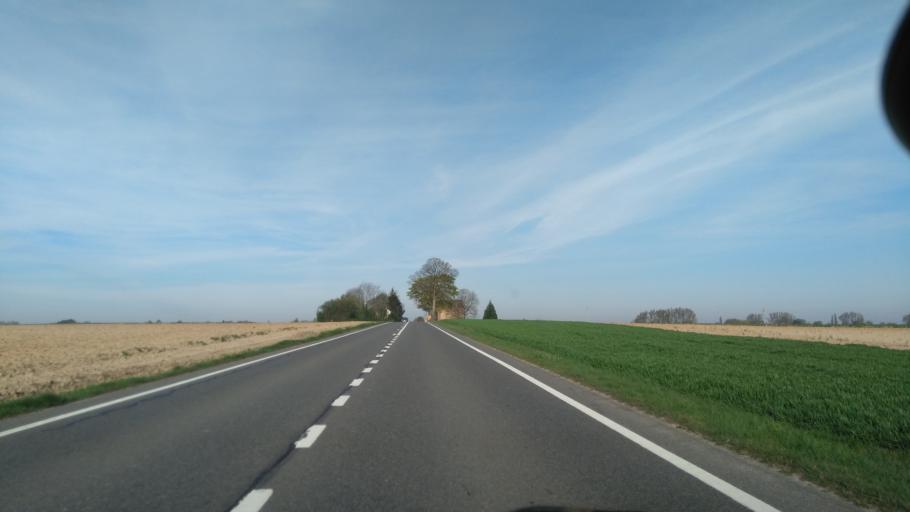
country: BE
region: Wallonia
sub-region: Province de Namur
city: Noville-les-Bois
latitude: 50.5825
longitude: 4.9636
